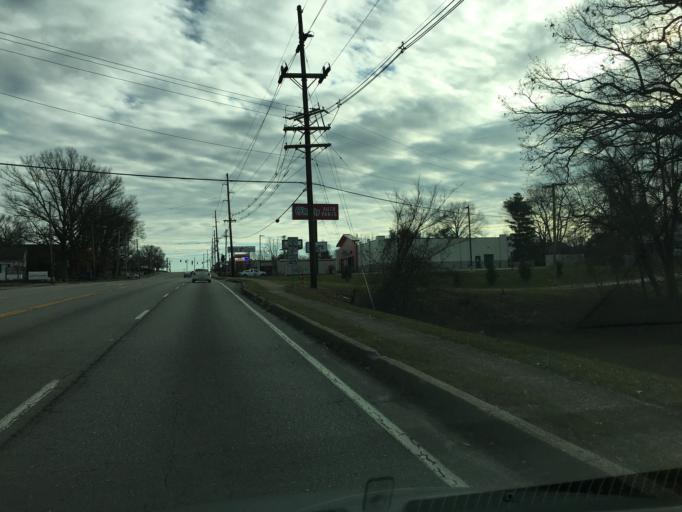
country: US
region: Kentucky
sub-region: Franklin County
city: Frankfort
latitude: 38.2007
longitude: -84.8321
